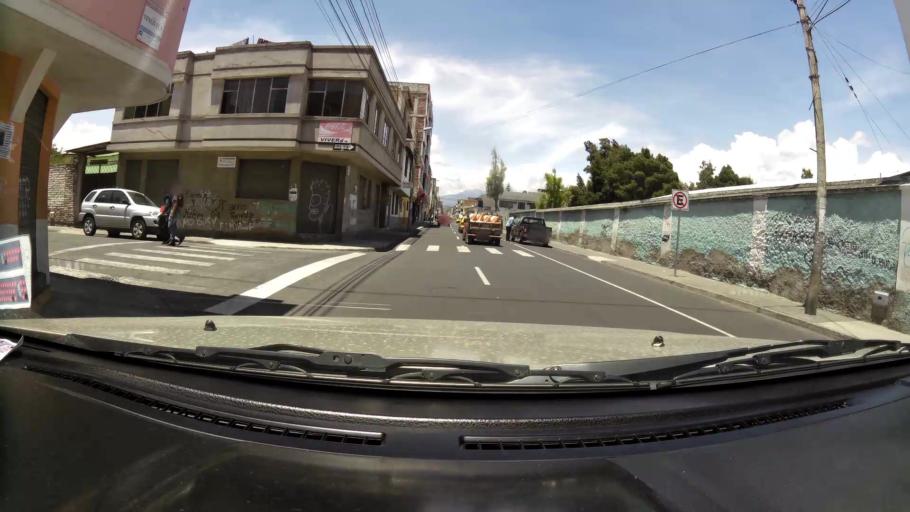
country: EC
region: Chimborazo
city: Riobamba
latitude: -1.6684
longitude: -78.6470
